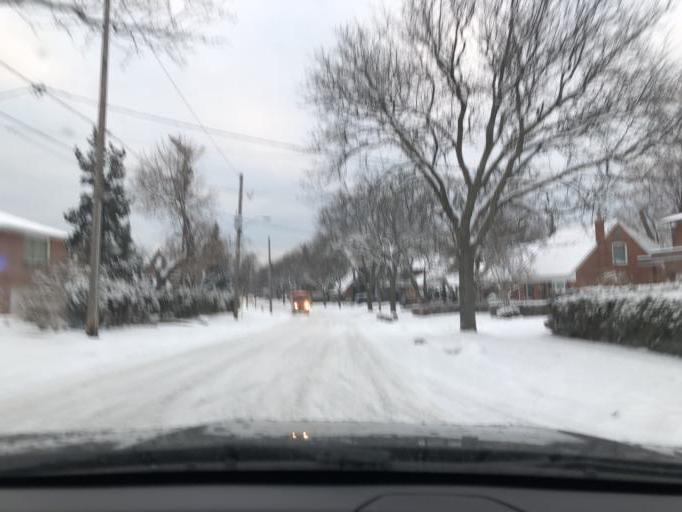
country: CA
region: Ontario
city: Toronto
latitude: 43.7025
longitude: -79.4816
